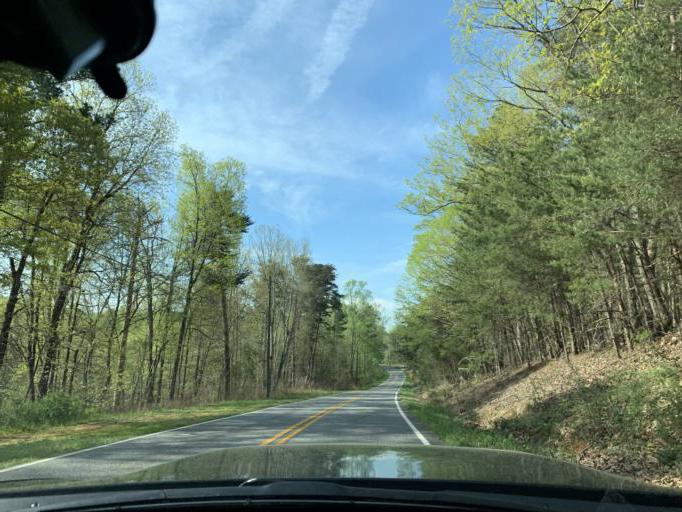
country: US
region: Georgia
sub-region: Forsyth County
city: Cumming
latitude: 34.2510
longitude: -84.1182
